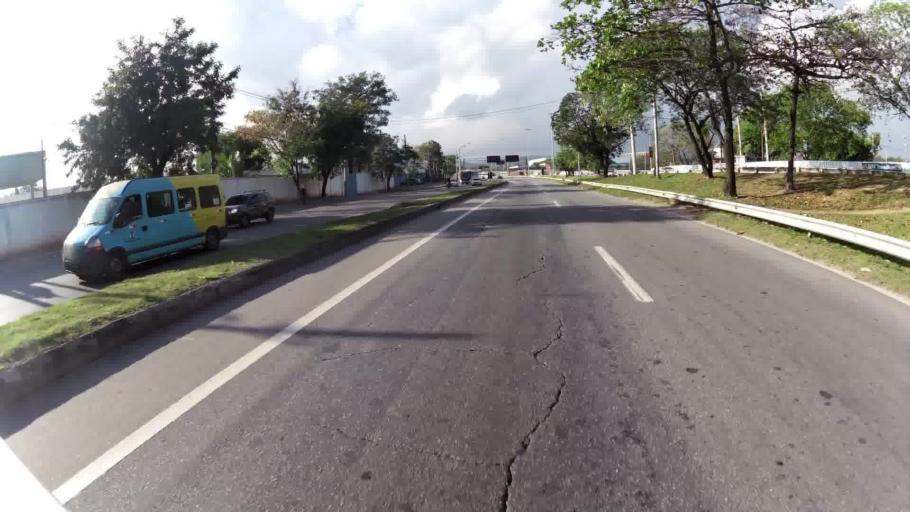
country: BR
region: Rio de Janeiro
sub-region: Duque De Caxias
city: Duque de Caxias
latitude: -22.8150
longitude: -43.2873
